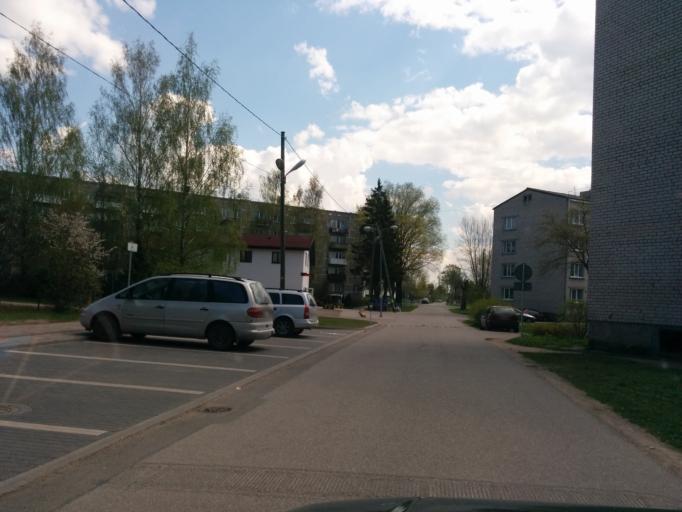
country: LV
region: Ozolnieku
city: Ozolnieki
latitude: 56.6482
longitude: 23.8107
